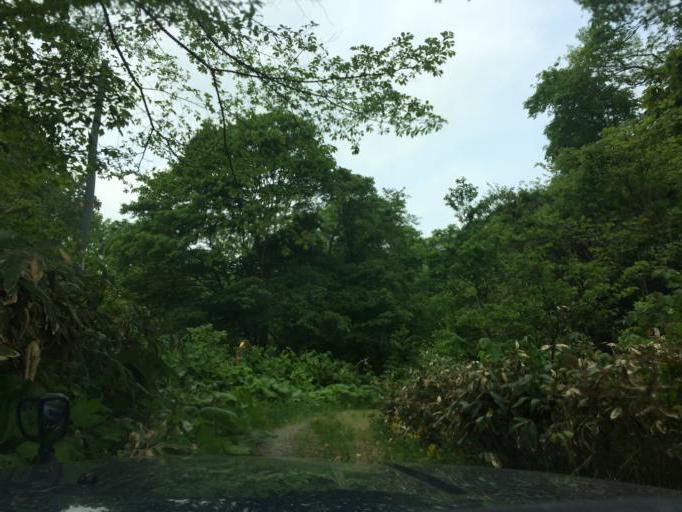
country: JP
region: Hokkaido
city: Niseko Town
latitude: 42.6340
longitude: 140.5776
